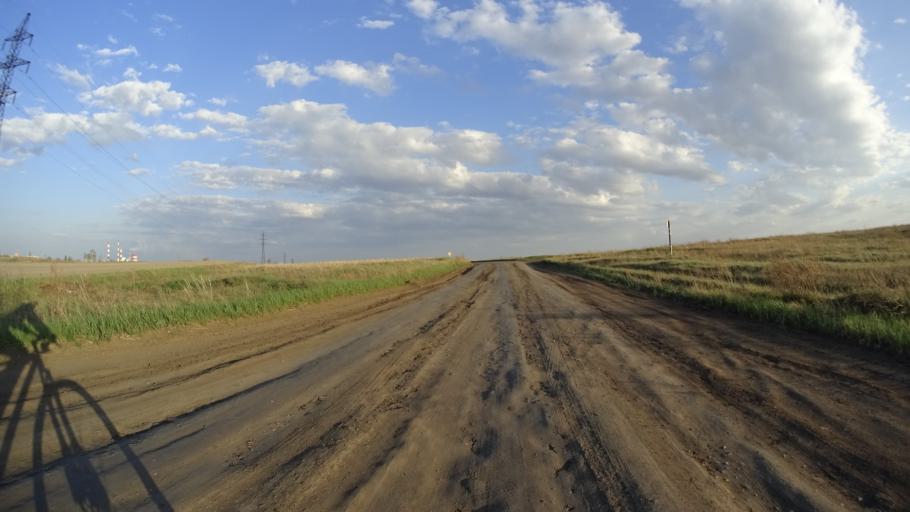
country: RU
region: Chelyabinsk
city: Troitsk
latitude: 54.0528
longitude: 61.5914
